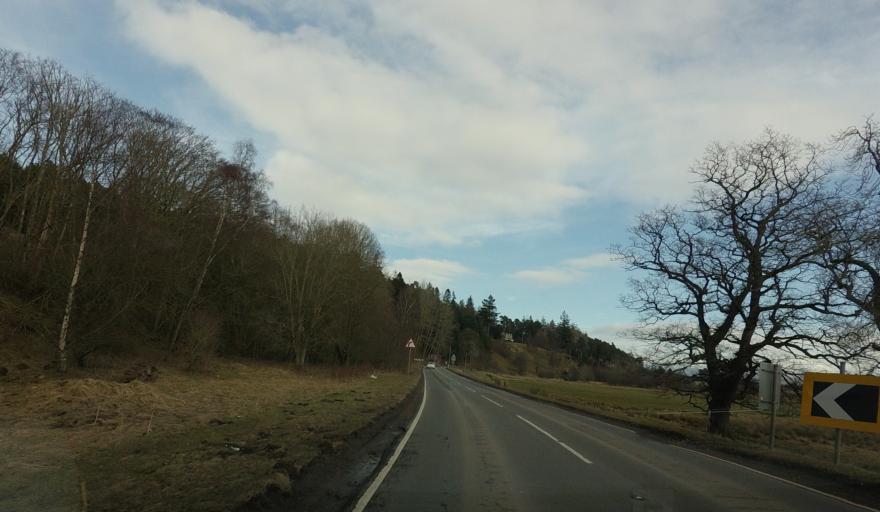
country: GB
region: Scotland
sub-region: Highland
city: Kingussie
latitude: 57.0767
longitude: -4.0703
